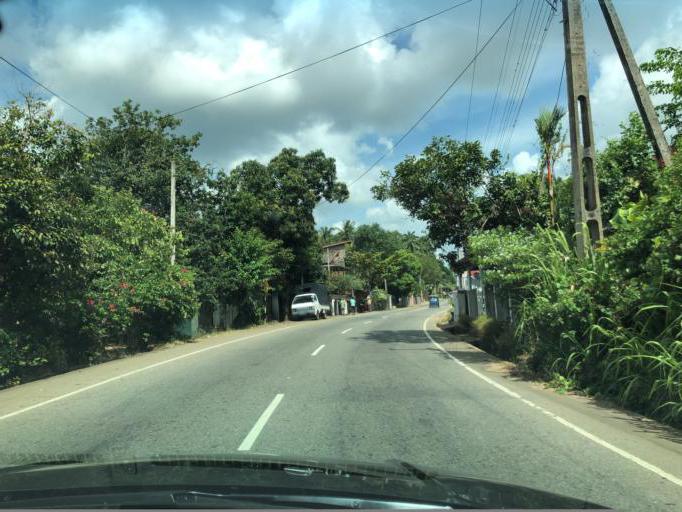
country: LK
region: Western
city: Horawala Junction
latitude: 6.5273
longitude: 80.1013
